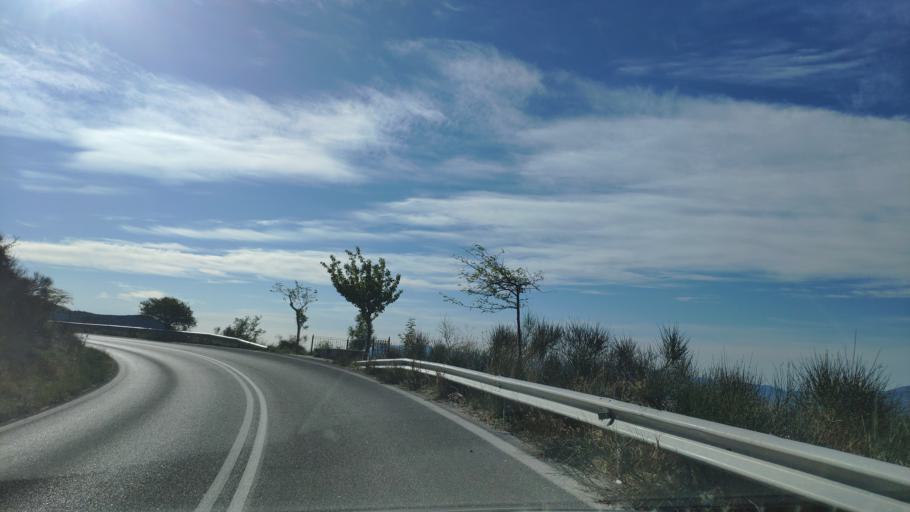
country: GR
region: Peloponnese
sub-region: Nomos Arkadias
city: Dimitsana
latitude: 37.5501
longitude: 22.0652
